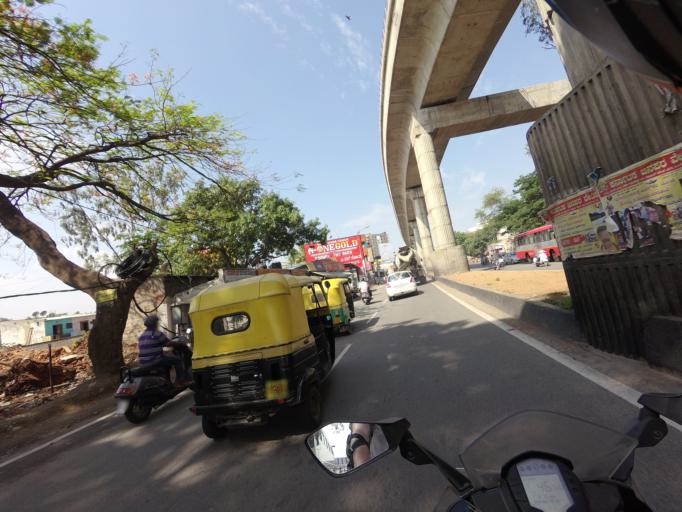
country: IN
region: Karnataka
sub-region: Bangalore Urban
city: Bangalore
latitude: 12.9501
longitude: 77.5373
